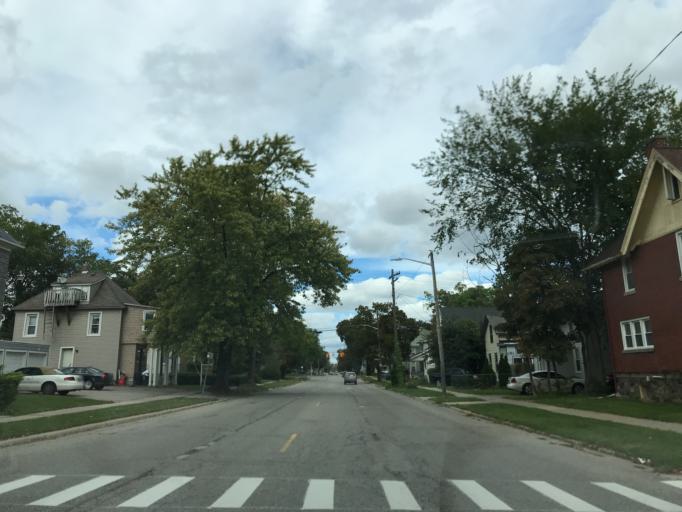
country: US
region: Michigan
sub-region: Washtenaw County
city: Ypsilanti
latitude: 42.2421
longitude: -83.6191
